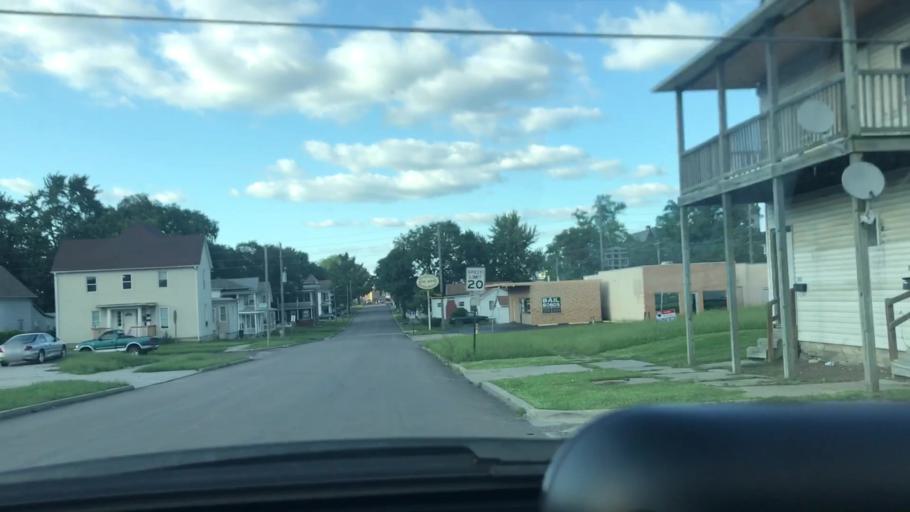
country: US
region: Missouri
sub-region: Pettis County
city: Sedalia
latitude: 38.7047
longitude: -93.2304
